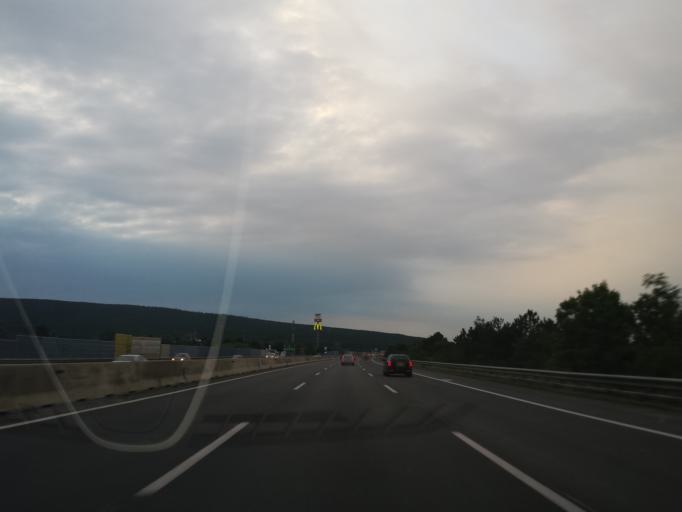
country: AT
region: Lower Austria
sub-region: Politischer Bezirk Wiener Neustadt
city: Weikersdorf am Steinfelde
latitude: 47.8302
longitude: 16.1838
